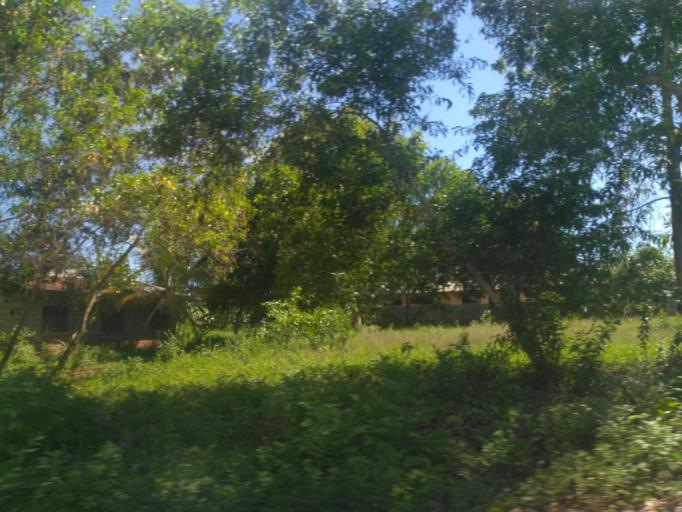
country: TZ
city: Kiwengwa
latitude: -5.9846
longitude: 39.3310
